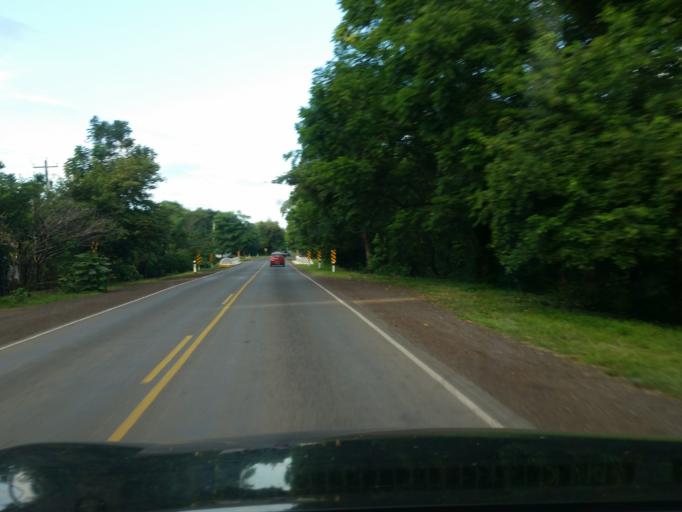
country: NI
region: Granada
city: Diriomo
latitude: 11.8252
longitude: -86.0385
